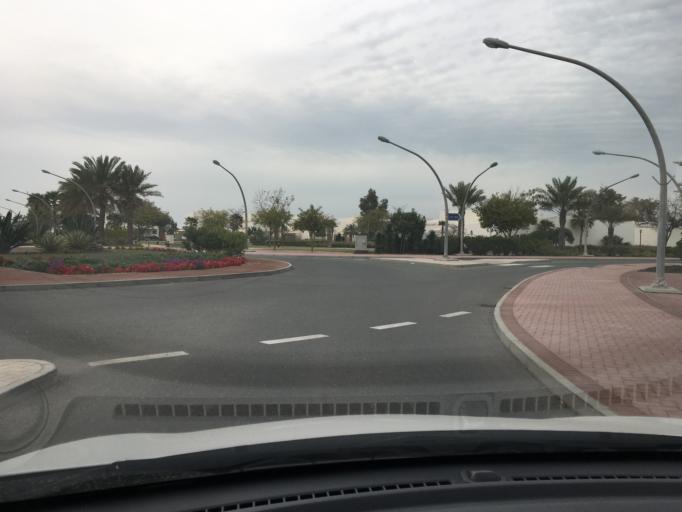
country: BH
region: Central Governorate
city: Dar Kulayb
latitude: 25.8389
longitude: 50.6152
